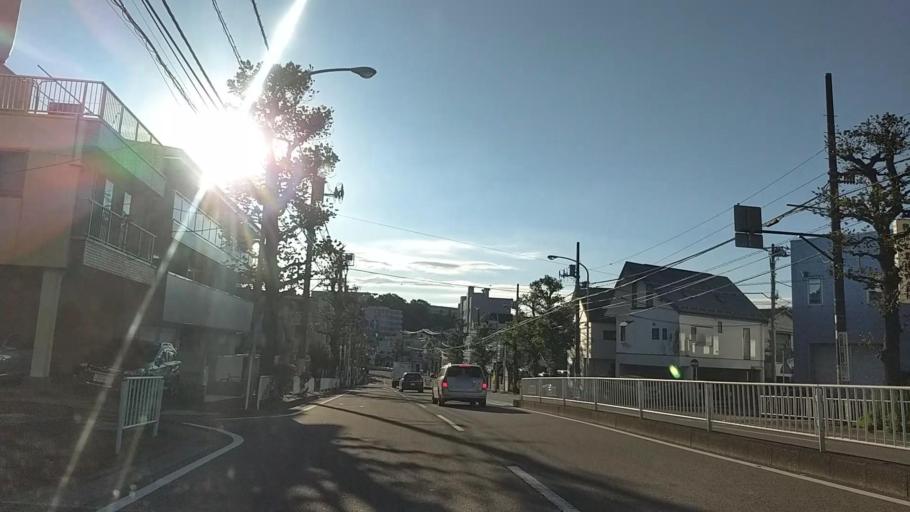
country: JP
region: Kanagawa
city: Yokohama
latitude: 35.4524
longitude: 139.6214
